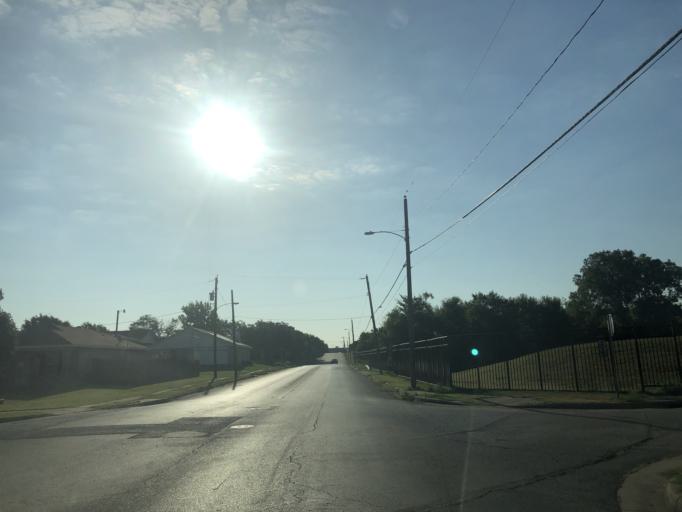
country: US
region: Texas
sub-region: Dallas County
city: Grand Prairie
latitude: 32.7350
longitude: -97.0276
